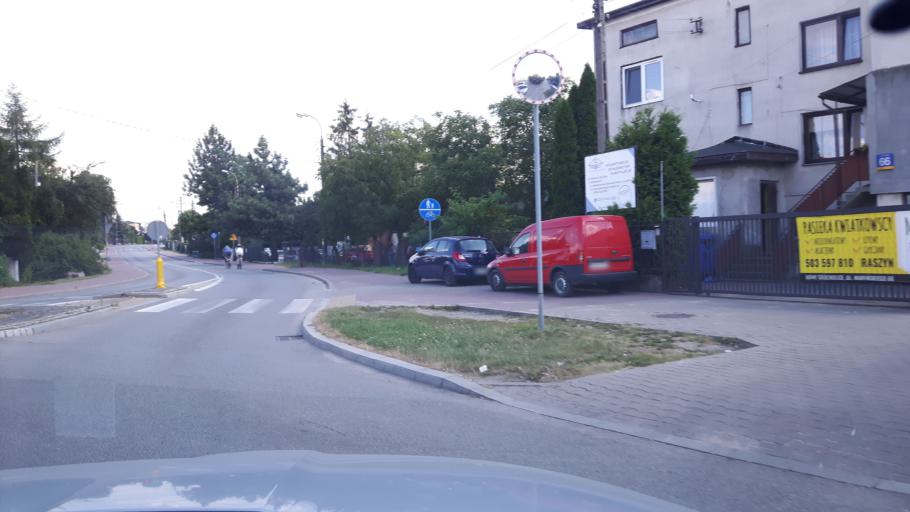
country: PL
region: Masovian Voivodeship
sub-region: Powiat pruszkowski
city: Nowe Grocholice
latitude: 52.1608
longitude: 20.9148
